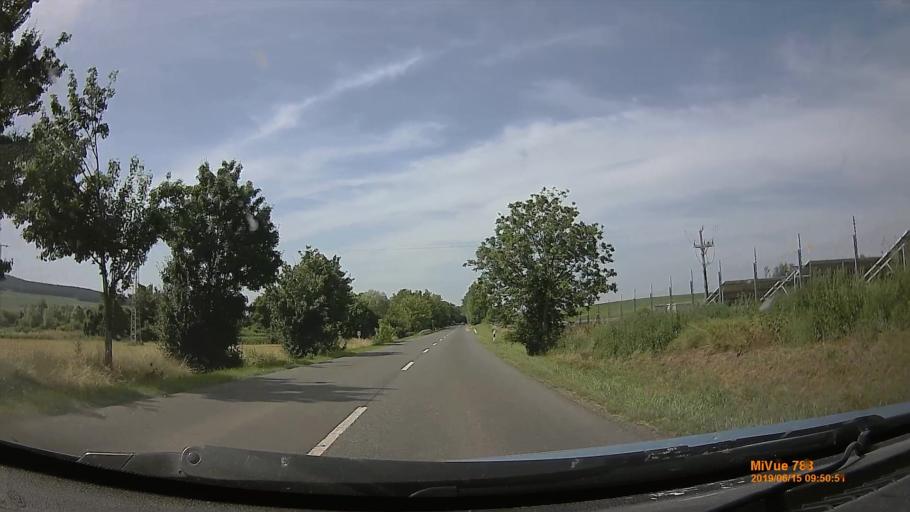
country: HU
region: Baranya
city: Sasd
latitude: 46.2915
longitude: 18.1216
